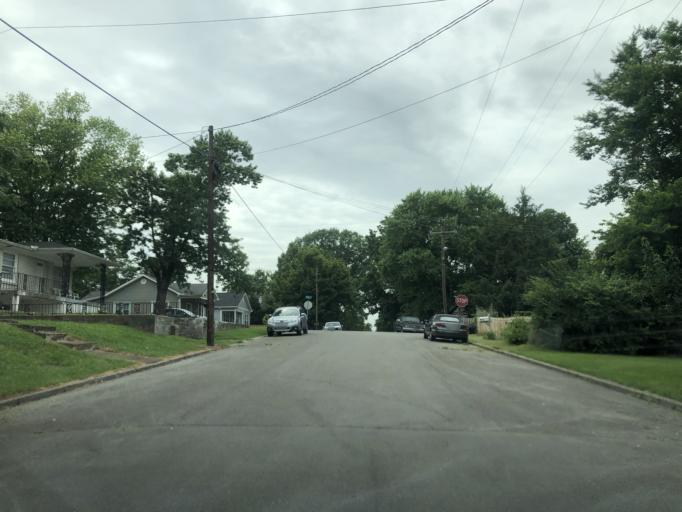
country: US
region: Tennessee
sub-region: Davidson County
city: Nashville
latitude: 36.1680
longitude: -86.7371
